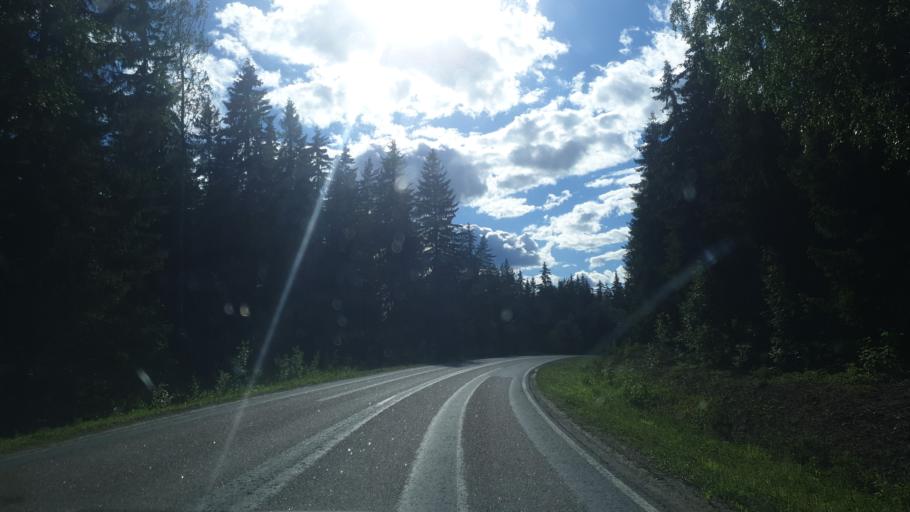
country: FI
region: Southern Savonia
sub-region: Mikkeli
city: Hirvensalmi
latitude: 61.5014
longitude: 26.7099
